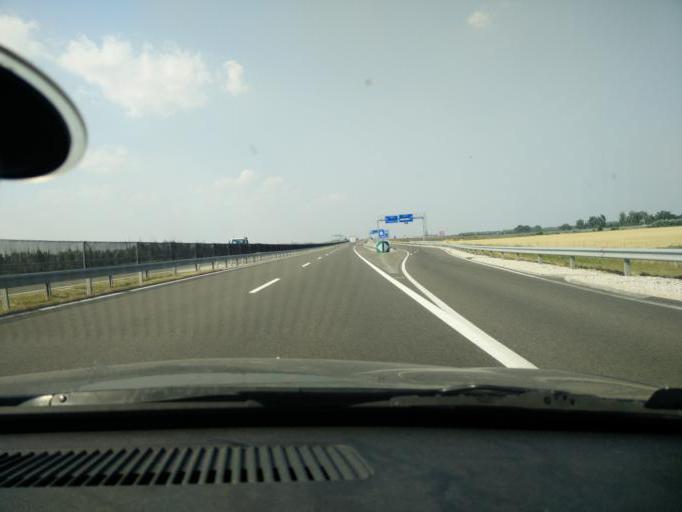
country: HU
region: Tolna
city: Szekszard
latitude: 46.3745
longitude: 18.7518
